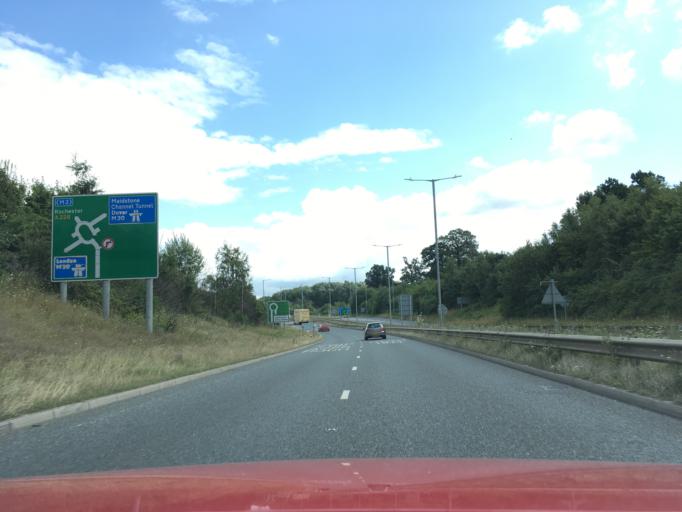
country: GB
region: England
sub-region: Kent
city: Larkfield
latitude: 51.3087
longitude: 0.4200
